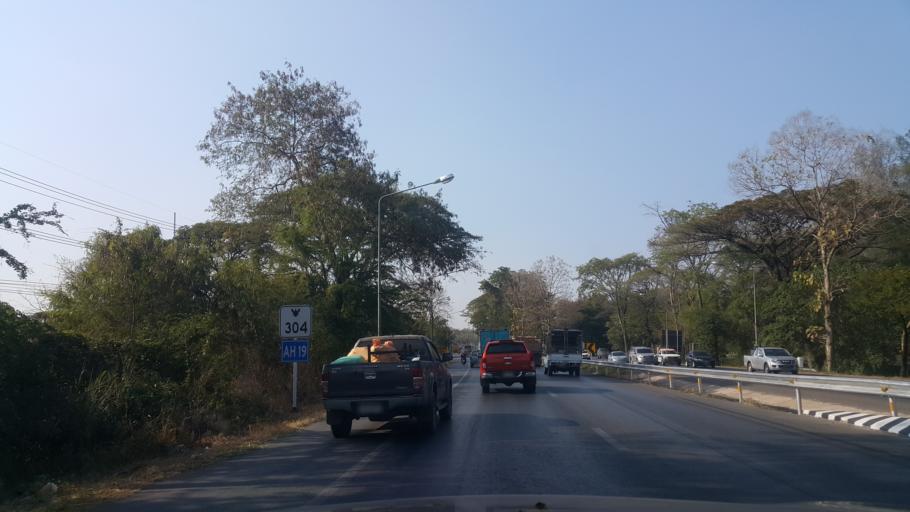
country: TH
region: Nakhon Ratchasima
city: Nakhon Ratchasima
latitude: 14.9171
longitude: 102.0651
